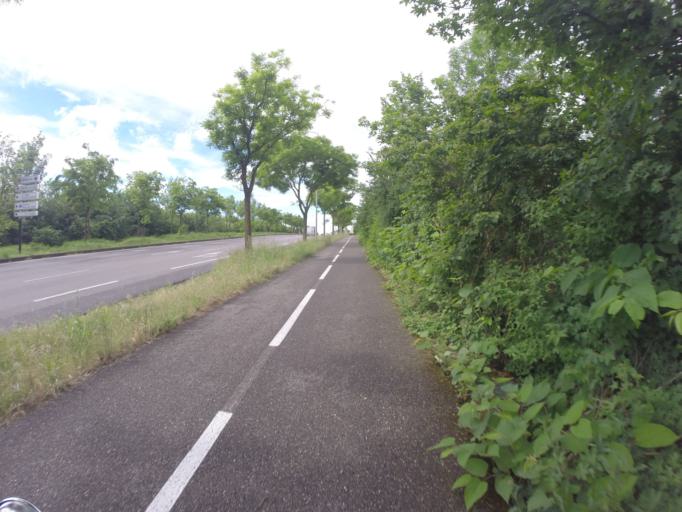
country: FR
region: Rhone-Alpes
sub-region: Departement du Rhone
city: Bron
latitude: 45.7288
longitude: 4.9283
